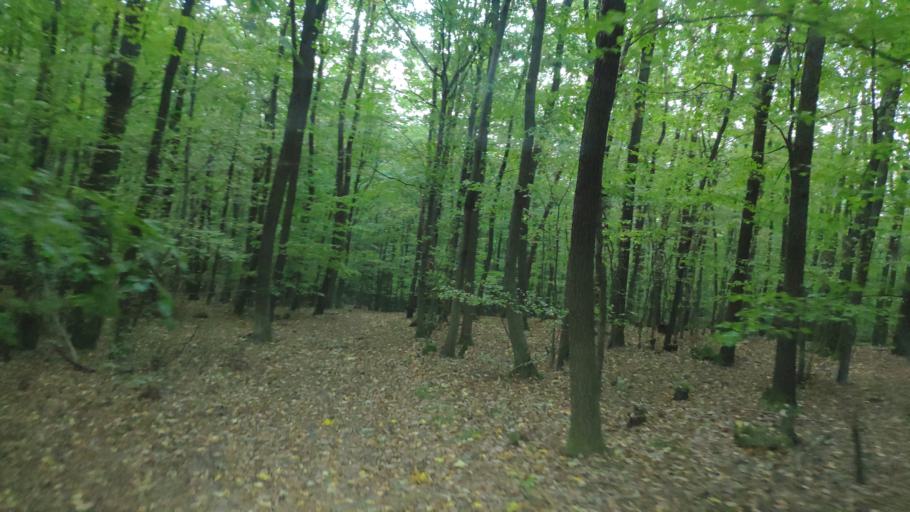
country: SK
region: Kosicky
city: Kosice
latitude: 48.6972
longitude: 21.1971
